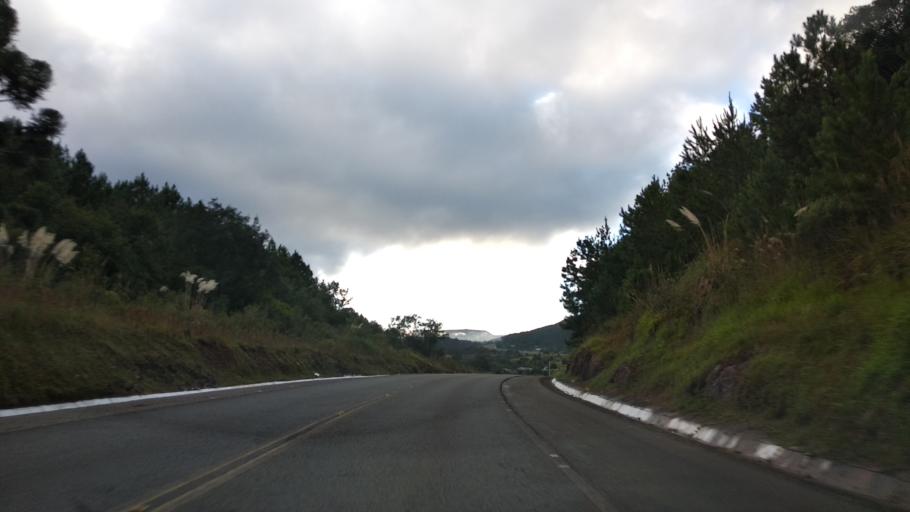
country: BR
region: Santa Catarina
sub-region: Curitibanos
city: Curitibanos
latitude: -27.5741
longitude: -50.7849
